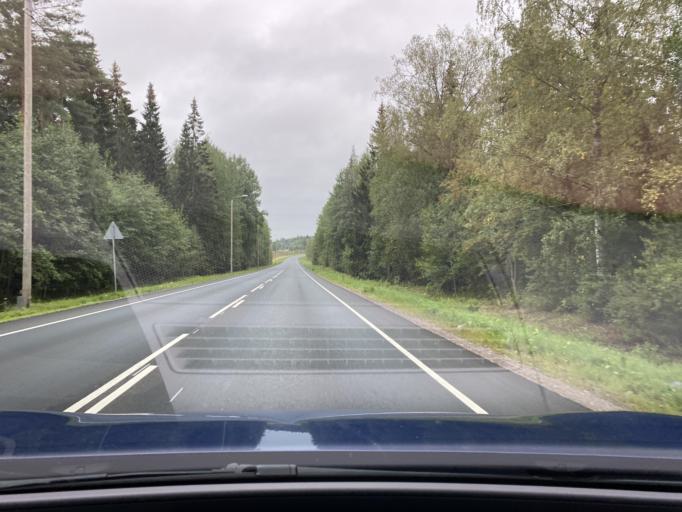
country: FI
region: Kymenlaakso
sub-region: Kouvola
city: Kouvola
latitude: 60.8927
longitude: 26.6042
